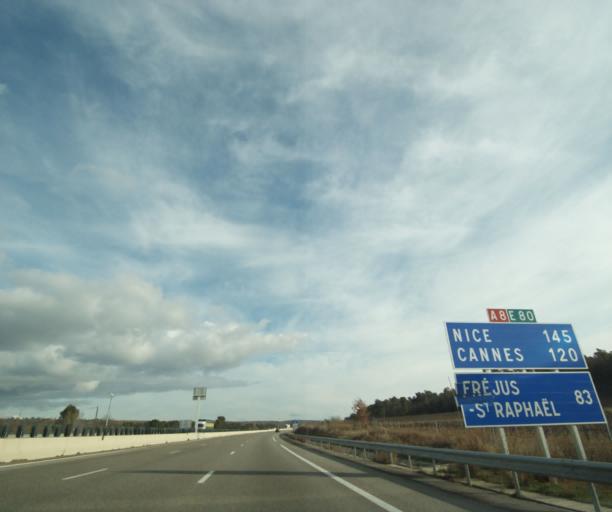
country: FR
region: Provence-Alpes-Cote d'Azur
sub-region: Departement du Var
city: Pourrieres
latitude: 43.4799
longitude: 5.7718
